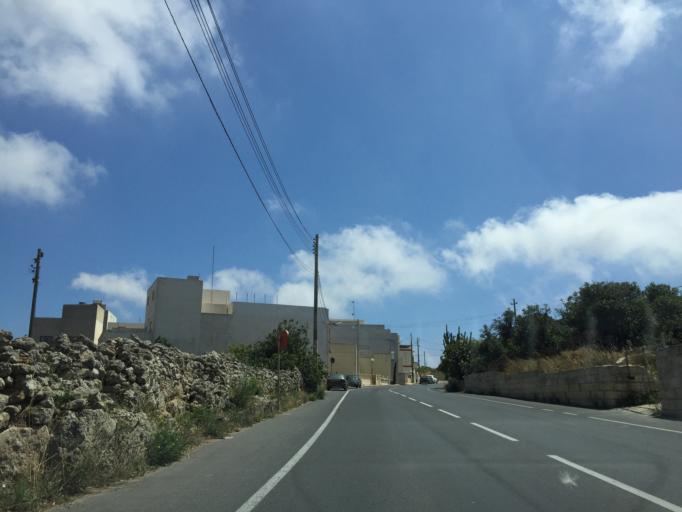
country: MT
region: Dingli
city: Dingli
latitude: 35.8656
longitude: 14.3897
